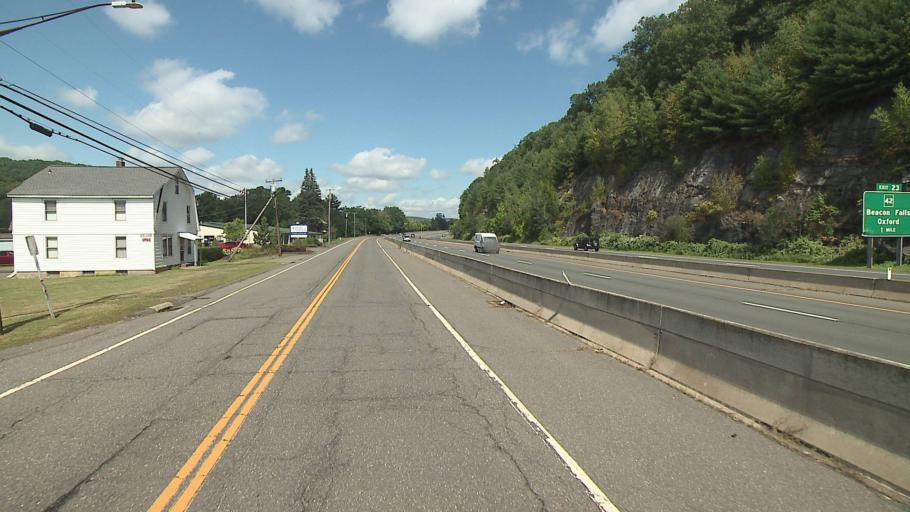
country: US
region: Connecticut
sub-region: New Haven County
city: Seymour
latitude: 41.4125
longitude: -73.0708
